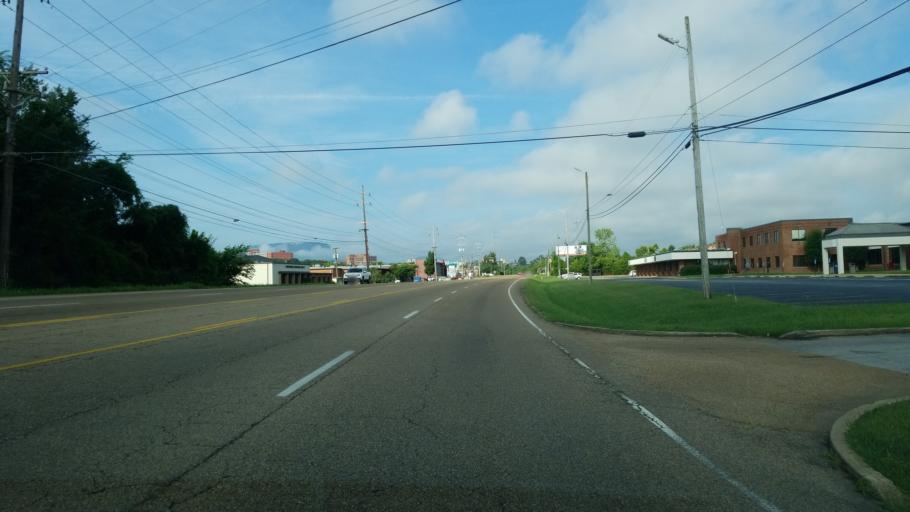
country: US
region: Tennessee
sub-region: Hamilton County
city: East Chattanooga
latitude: 35.0568
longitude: -85.2783
